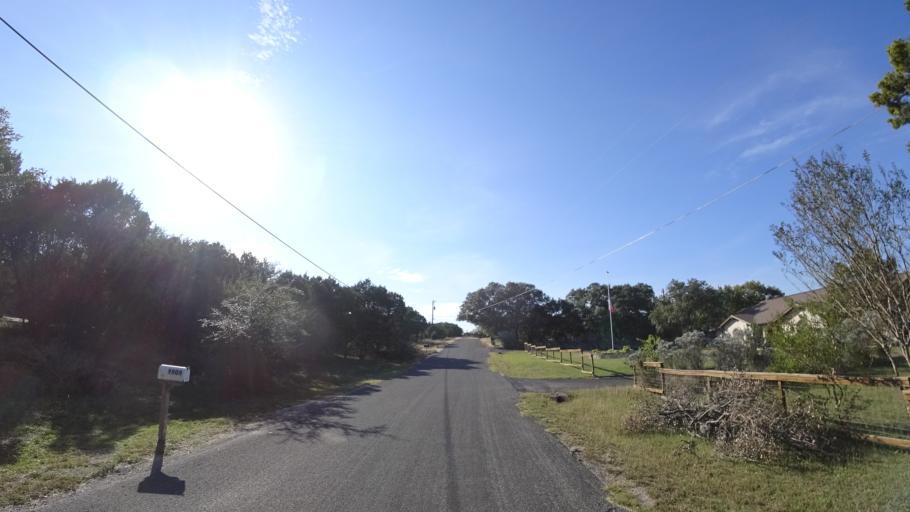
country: US
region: Texas
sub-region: Travis County
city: Bee Cave
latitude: 30.2350
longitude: -97.9274
